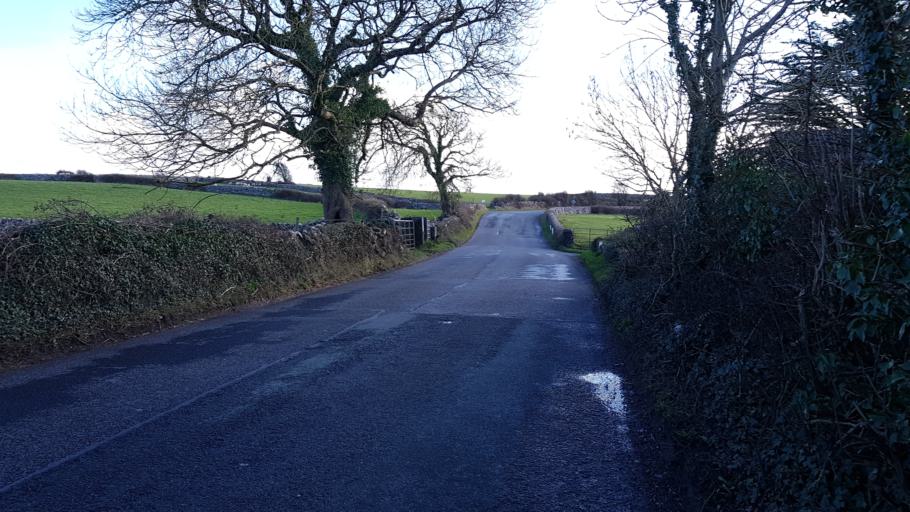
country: IE
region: Connaught
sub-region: County Galway
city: Gaillimh
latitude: 53.3080
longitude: -9.0201
